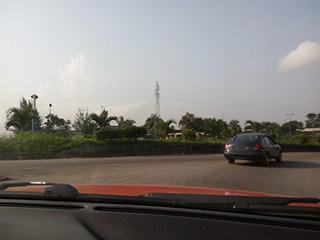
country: CI
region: Lagunes
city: Abidjan
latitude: 5.3550
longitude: -3.9918
